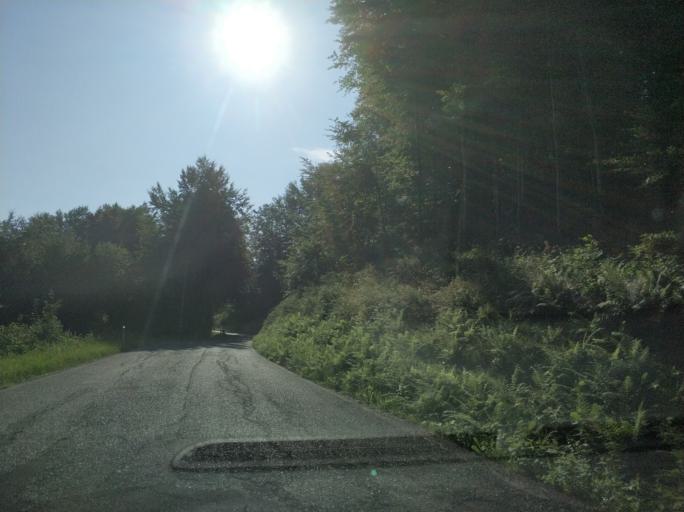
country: IT
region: Piedmont
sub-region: Provincia di Torino
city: Viu
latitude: 45.2085
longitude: 7.3750
